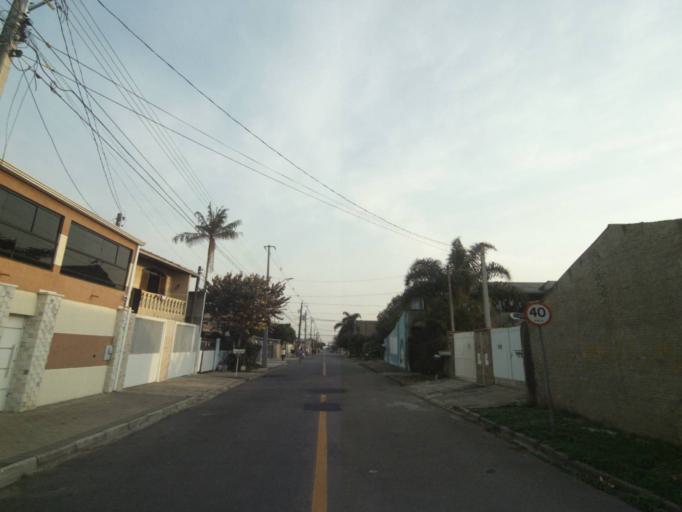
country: BR
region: Parana
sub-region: Pinhais
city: Pinhais
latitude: -25.4852
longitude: -49.2015
